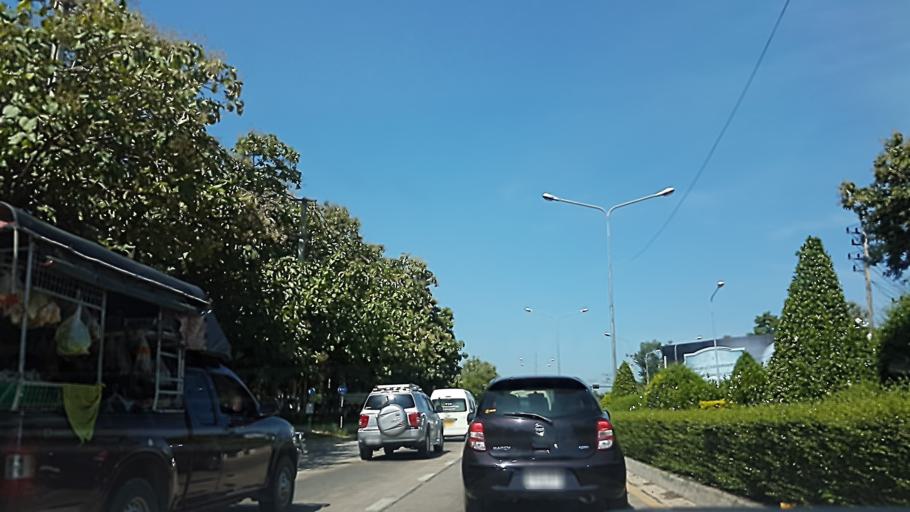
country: TH
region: Chiang Mai
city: Chiang Mai
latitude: 18.8389
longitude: 98.9742
